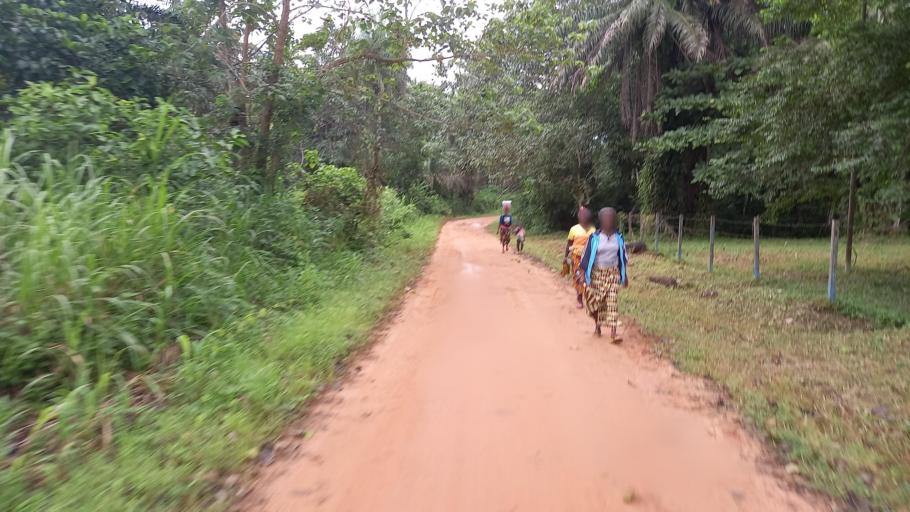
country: SL
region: Eastern Province
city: Kailahun
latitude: 8.2417
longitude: -10.5185
